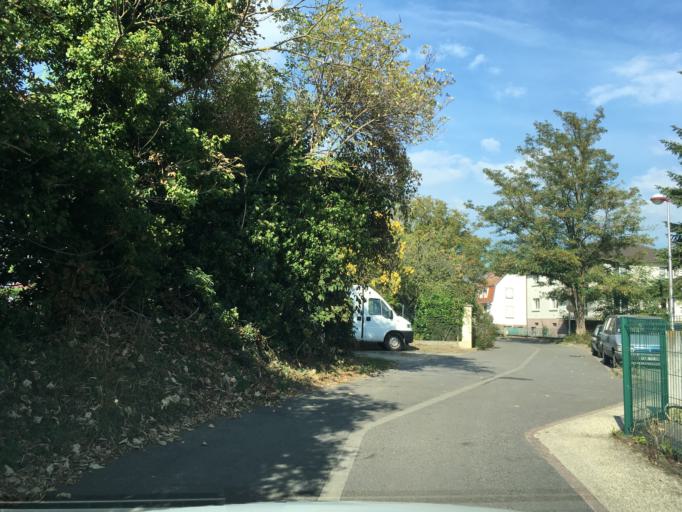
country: FR
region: Alsace
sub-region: Departement du Haut-Rhin
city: Colmar
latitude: 48.0704
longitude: 7.3753
